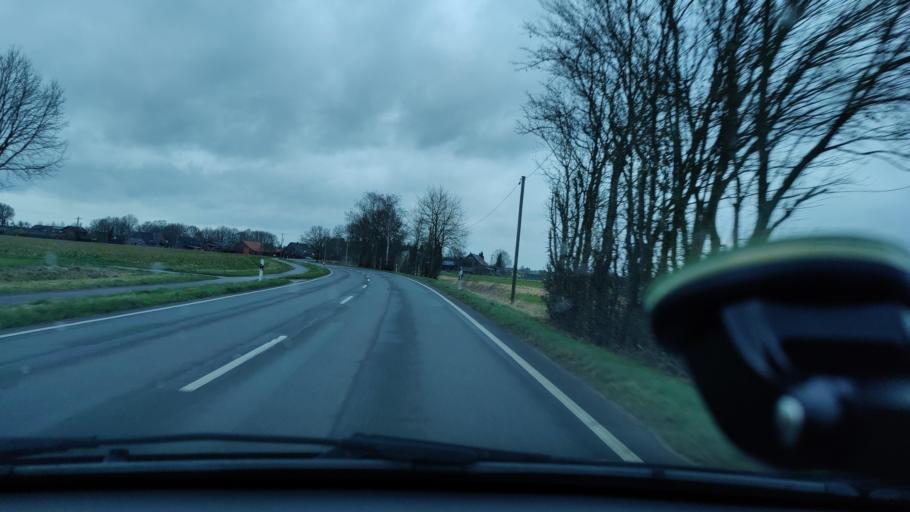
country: DE
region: North Rhine-Westphalia
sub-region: Regierungsbezirk Dusseldorf
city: Weeze
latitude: 51.5756
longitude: 6.1838
